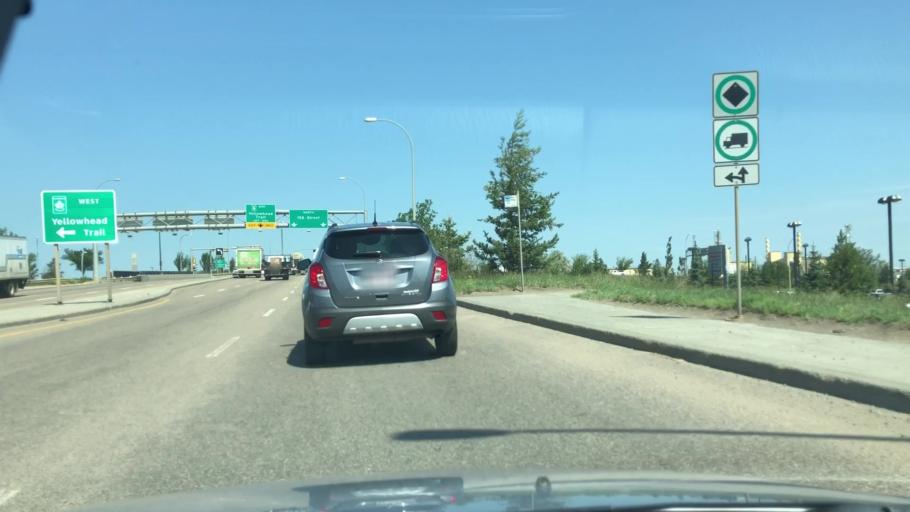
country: CA
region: Alberta
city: St. Albert
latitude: 53.5777
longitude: -113.5903
